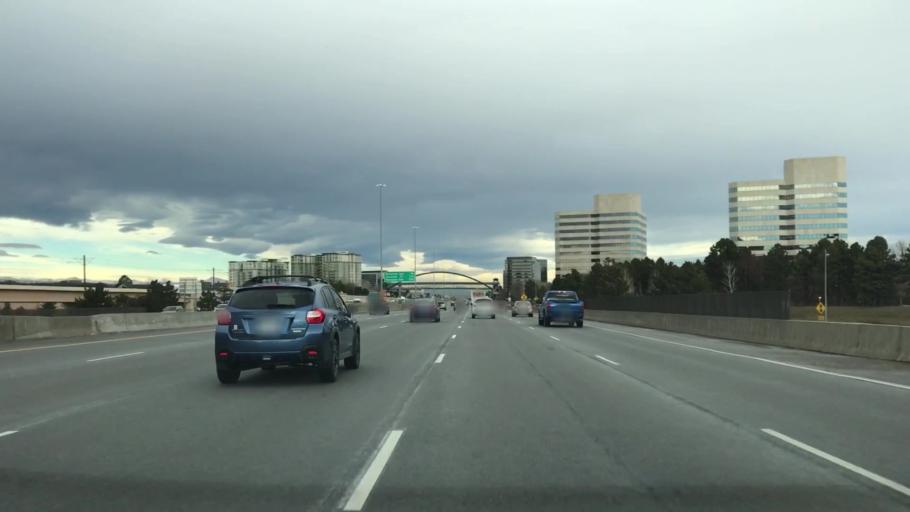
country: US
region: Colorado
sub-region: Arapahoe County
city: Castlewood
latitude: 39.6091
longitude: -104.8924
